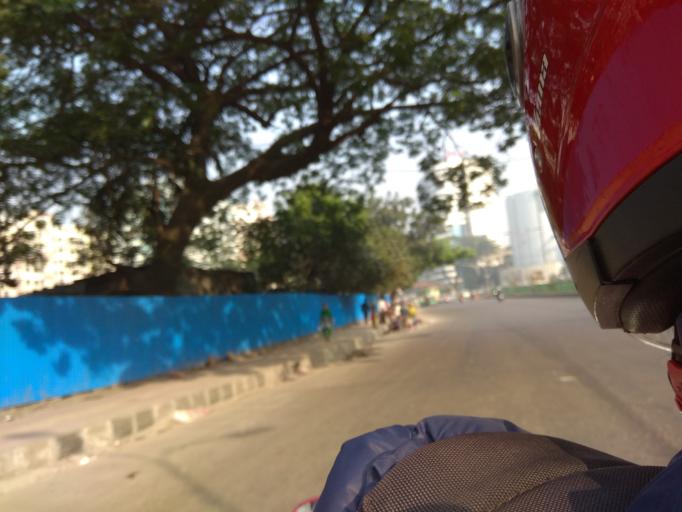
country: BD
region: Dhaka
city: Azimpur
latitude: 23.7404
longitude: 90.3960
